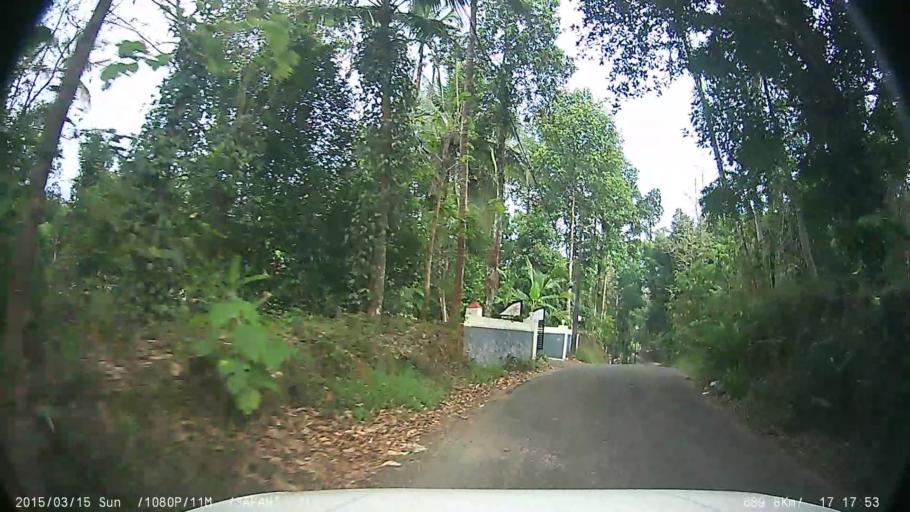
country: IN
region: Kerala
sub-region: Kottayam
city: Palackattumala
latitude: 9.8567
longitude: 76.6953
